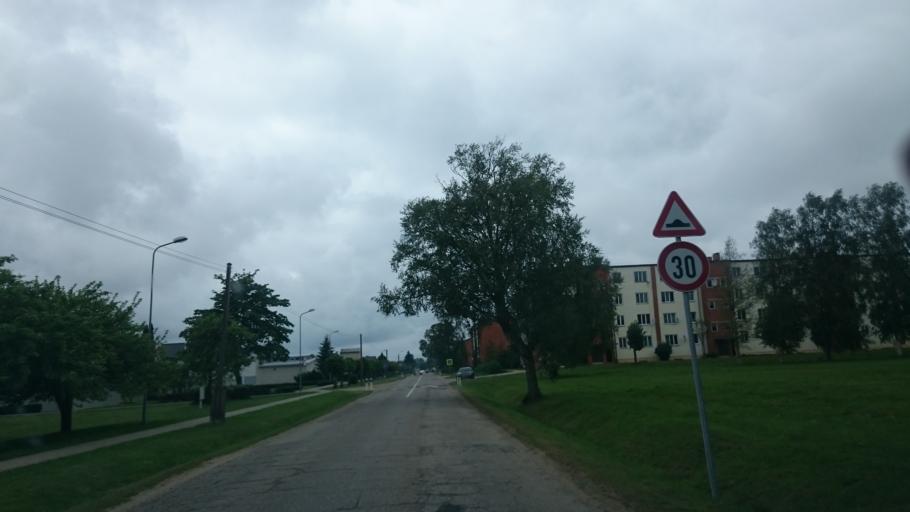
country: LV
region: Pavilostas
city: Pavilosta
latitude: 56.8828
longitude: 21.2047
